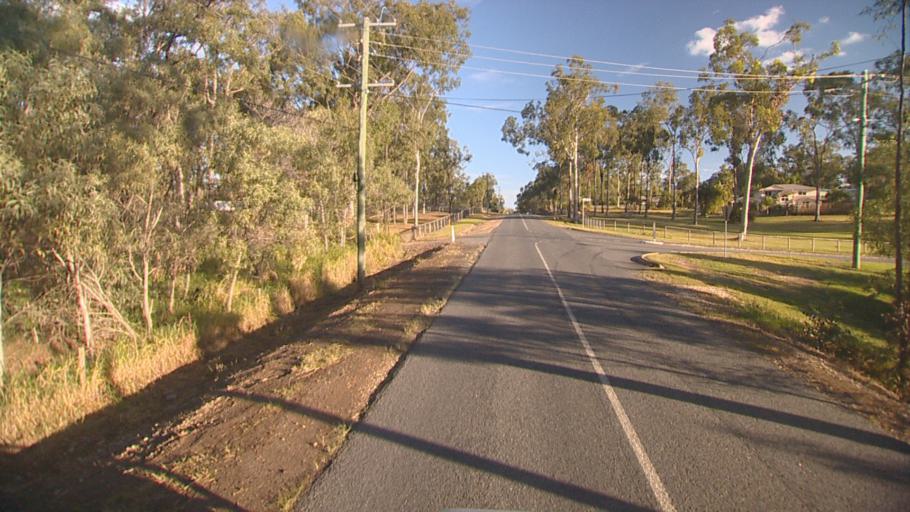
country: AU
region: Queensland
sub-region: Logan
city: Waterford West
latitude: -27.7306
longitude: 153.1463
